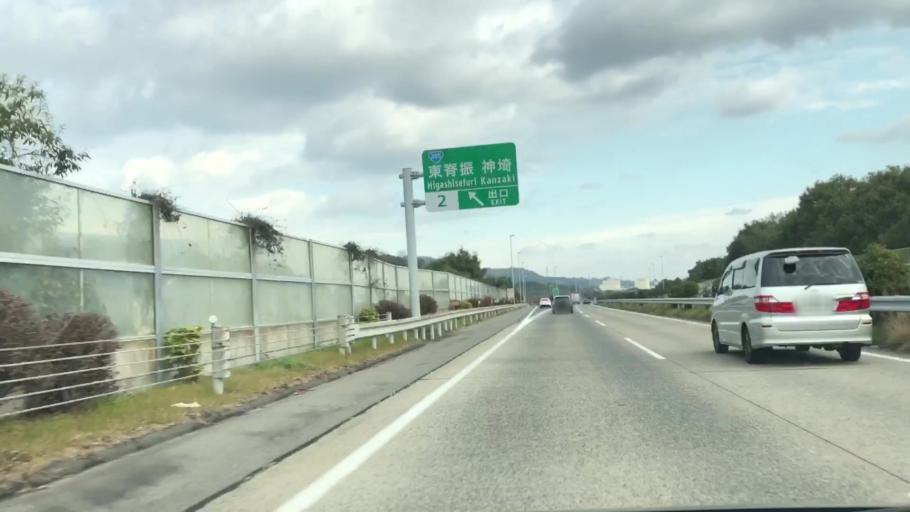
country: JP
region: Saga Prefecture
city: Kanzakimachi-kanzaki
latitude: 33.3535
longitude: 130.3907
